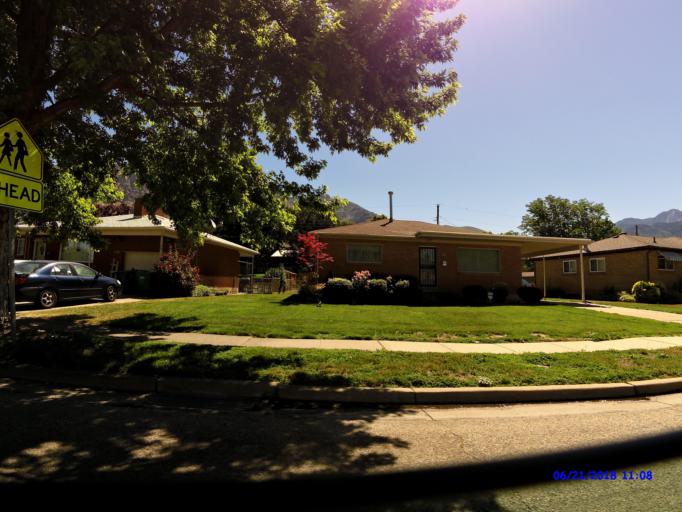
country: US
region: Utah
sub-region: Weber County
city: Ogden
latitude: 41.2543
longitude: -111.9552
